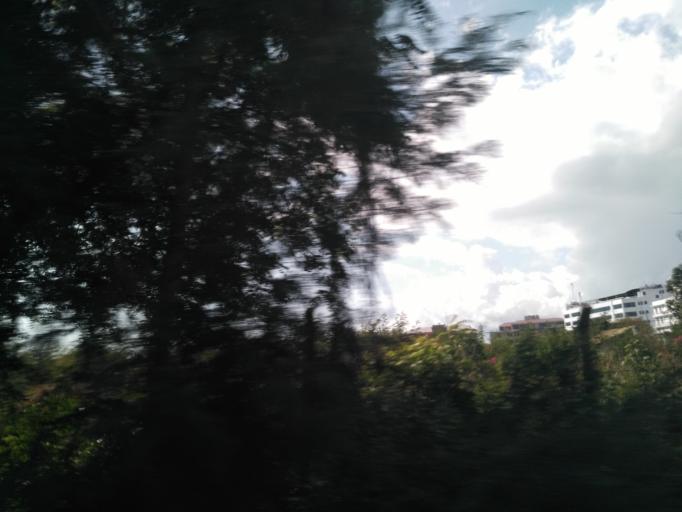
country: TZ
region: Dar es Salaam
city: Magomeni
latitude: -6.7427
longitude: 39.2798
